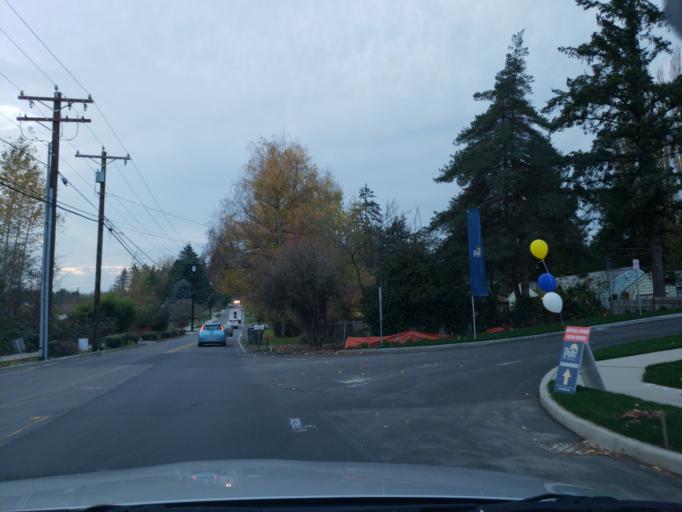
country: US
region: Washington
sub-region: King County
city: Bothell
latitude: 47.7803
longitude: -122.2236
